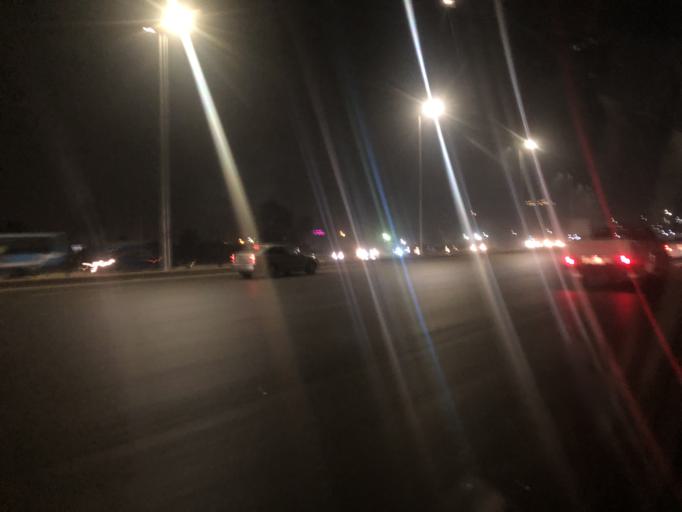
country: EG
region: Al Jizah
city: Al Jizah
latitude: 29.9872
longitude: 31.1274
